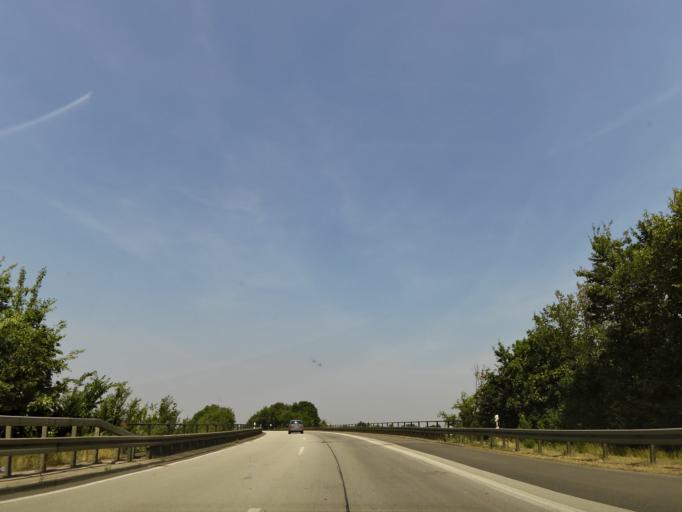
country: DE
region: North Rhine-Westphalia
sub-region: Regierungsbezirk Koln
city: Erftstadt
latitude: 50.8159
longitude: 6.7872
